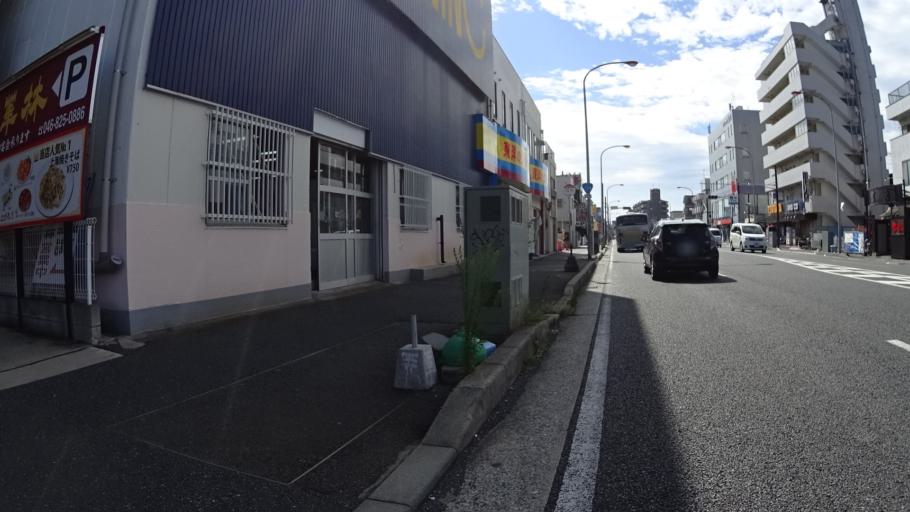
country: JP
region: Kanagawa
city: Yokosuka
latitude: 35.2662
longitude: 139.6878
